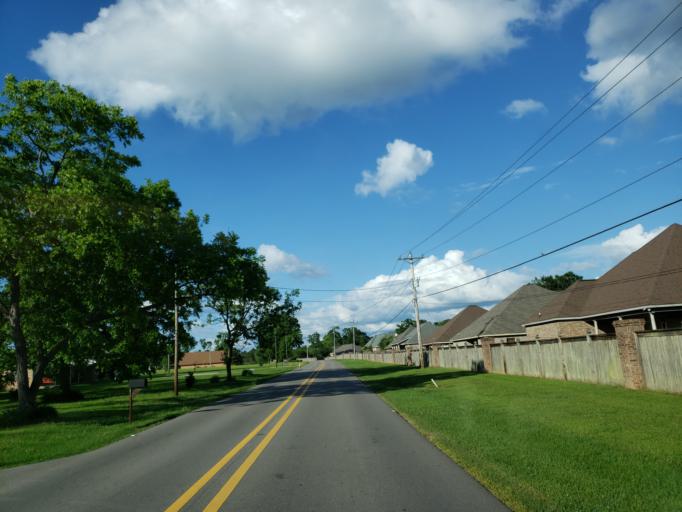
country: US
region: Mississippi
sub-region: Forrest County
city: Petal
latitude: 31.3446
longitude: -89.2338
